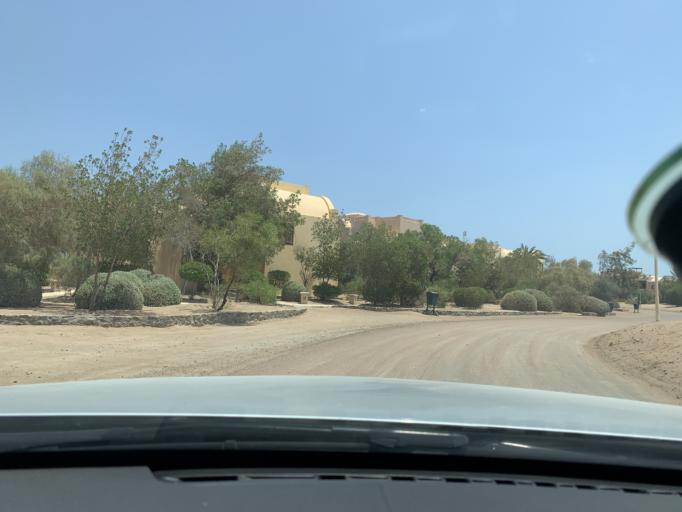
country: EG
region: Red Sea
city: El Gouna
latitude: 27.4017
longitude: 33.6725
